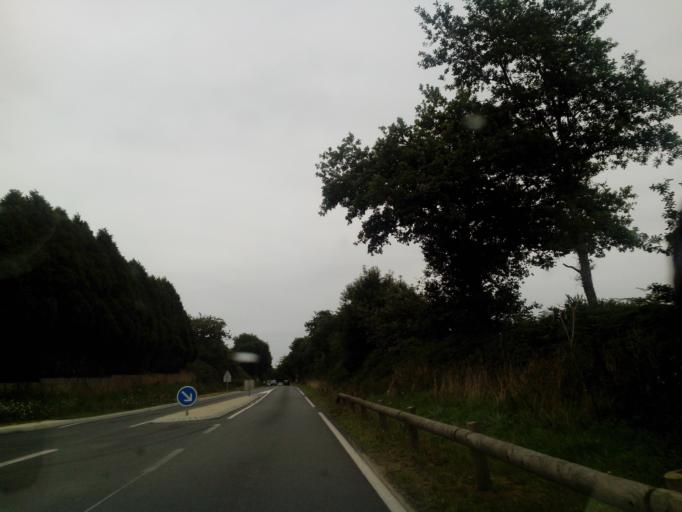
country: FR
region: Brittany
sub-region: Departement du Finistere
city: Quimperle
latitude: 47.8555
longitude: -3.5136
